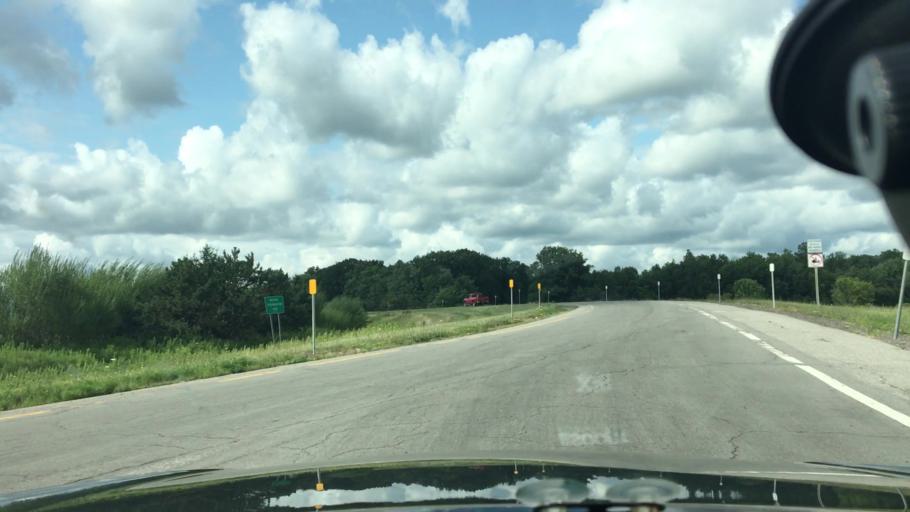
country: US
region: New York
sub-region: Erie County
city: North Boston
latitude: 42.6942
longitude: -78.7843
